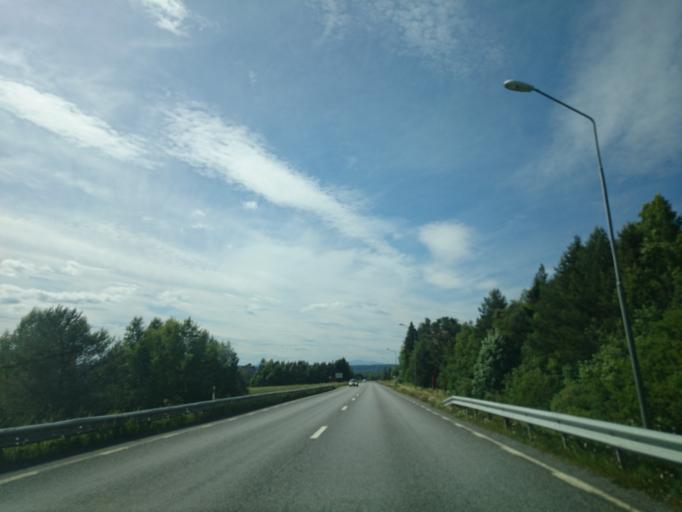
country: SE
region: Jaemtland
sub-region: Krokoms Kommun
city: Valla
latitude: 63.3185
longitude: 14.0817
